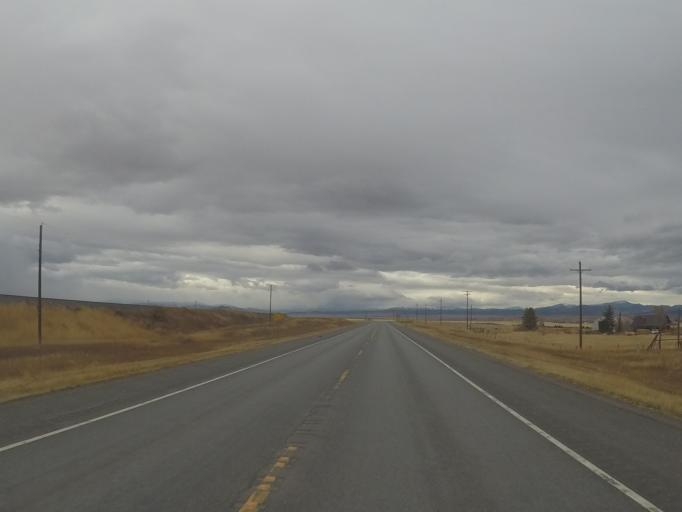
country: US
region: Montana
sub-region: Lewis and Clark County
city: East Helena
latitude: 46.5578
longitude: -111.7760
